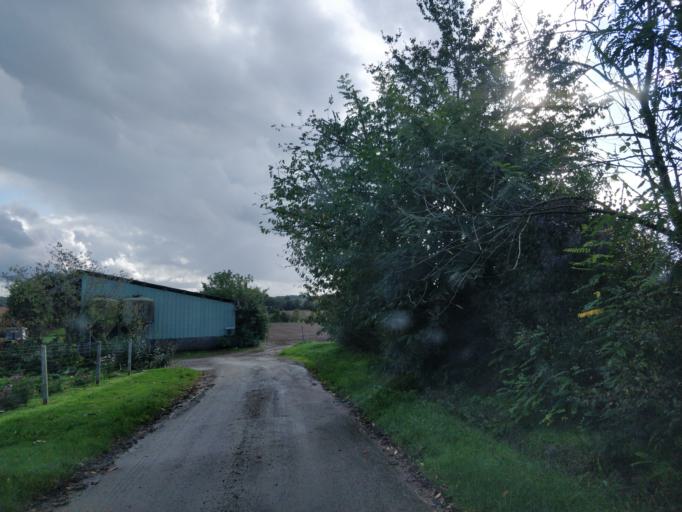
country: FR
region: Brittany
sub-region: Departement d'Ille-et-Vilaine
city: Chateaubourg
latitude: 48.1187
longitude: -1.4291
